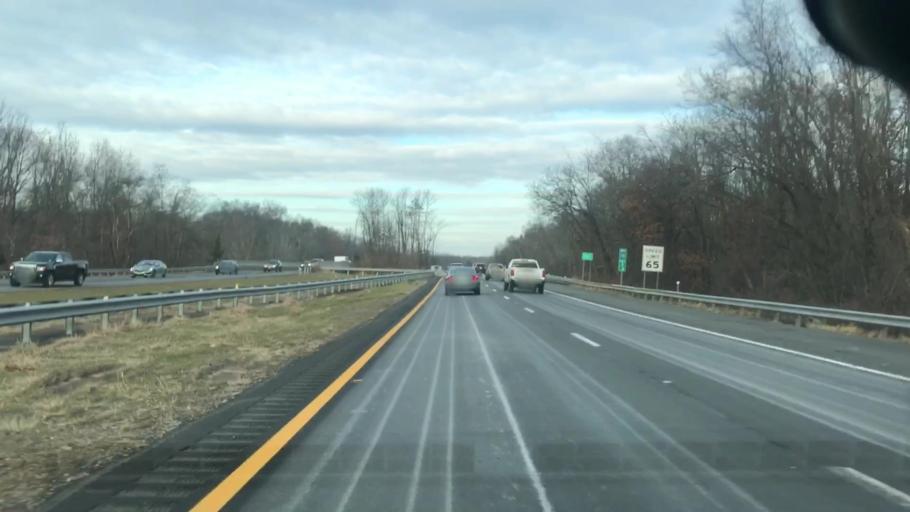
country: US
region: New Jersey
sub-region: Essex County
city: West Caldwell
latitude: 40.8295
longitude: -74.3277
